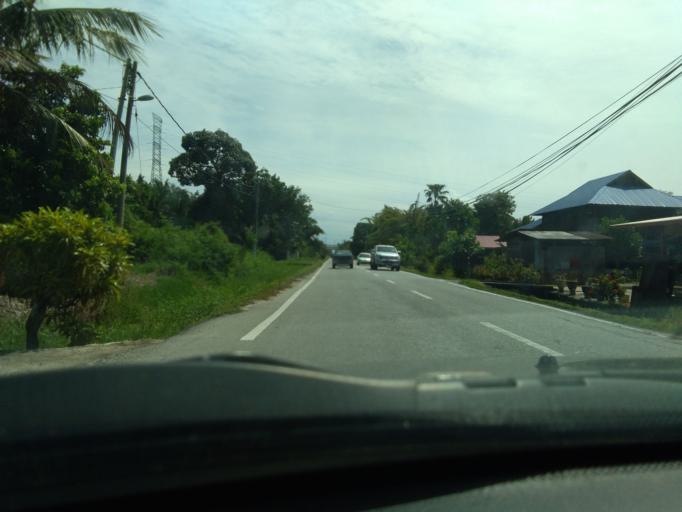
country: MY
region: Perak
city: Bagan Serai
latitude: 5.0162
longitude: 100.5416
